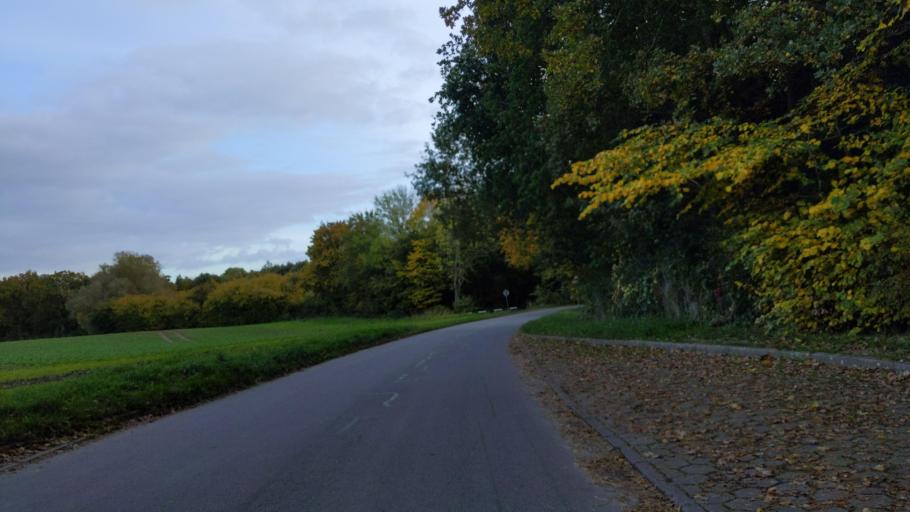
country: DE
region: Schleswig-Holstein
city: Sierksdorf
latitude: 54.0877
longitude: 10.7459
